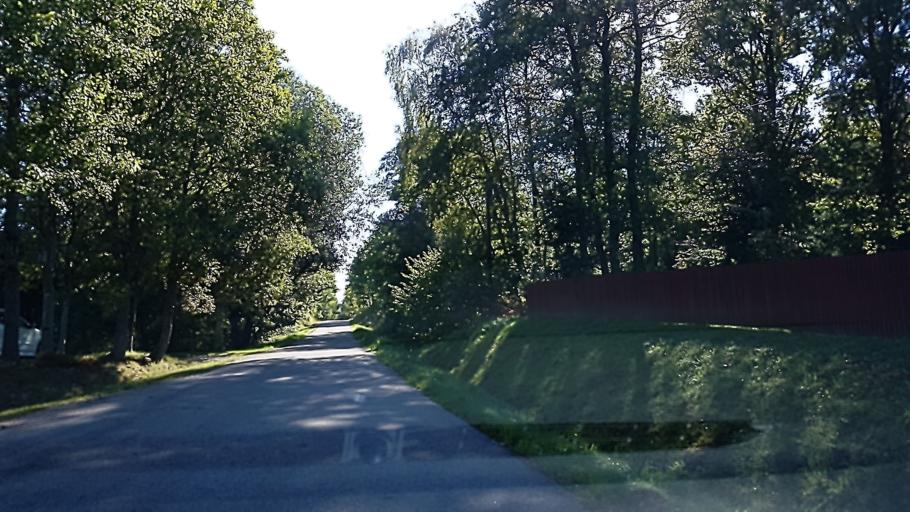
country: SE
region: Kronoberg
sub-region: Ljungby Kommun
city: Ljungby
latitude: 56.8113
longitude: 14.0042
